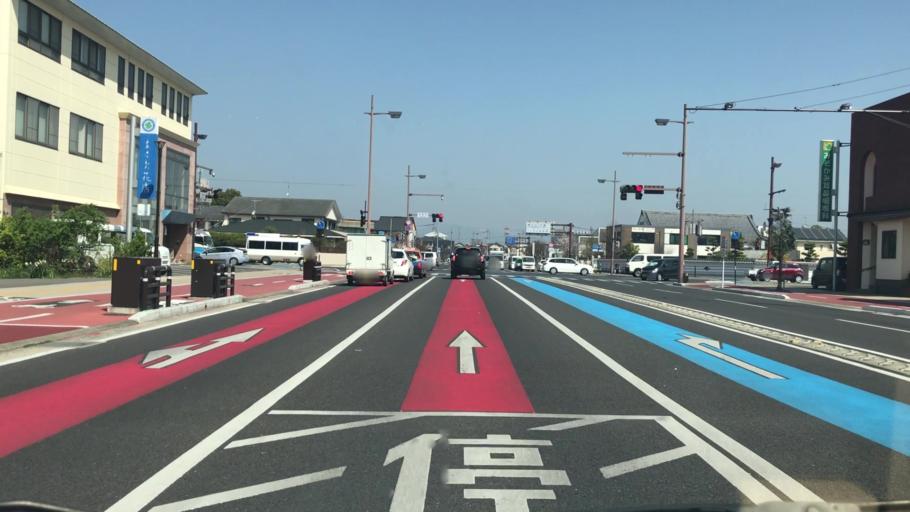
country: JP
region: Saga Prefecture
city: Saga-shi
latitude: 33.2494
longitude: 130.2926
